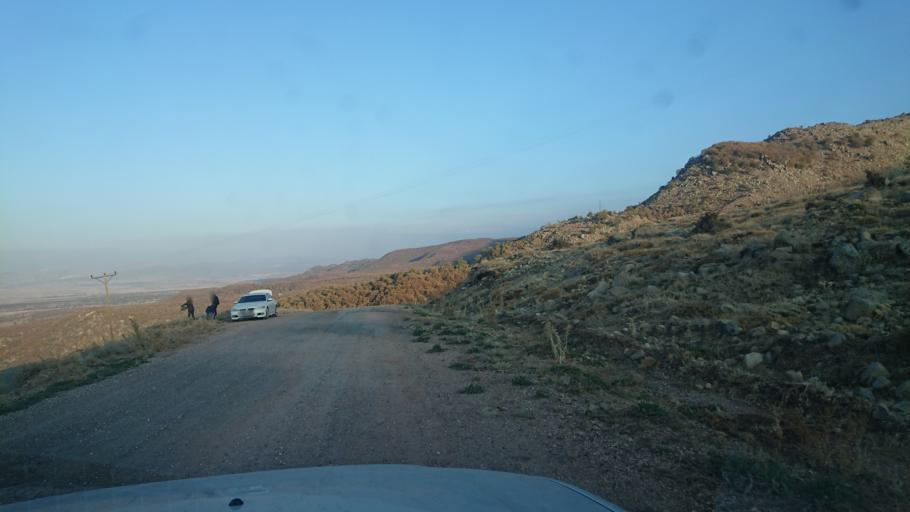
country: TR
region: Aksaray
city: Taspinar
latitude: 38.1662
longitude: 34.1794
